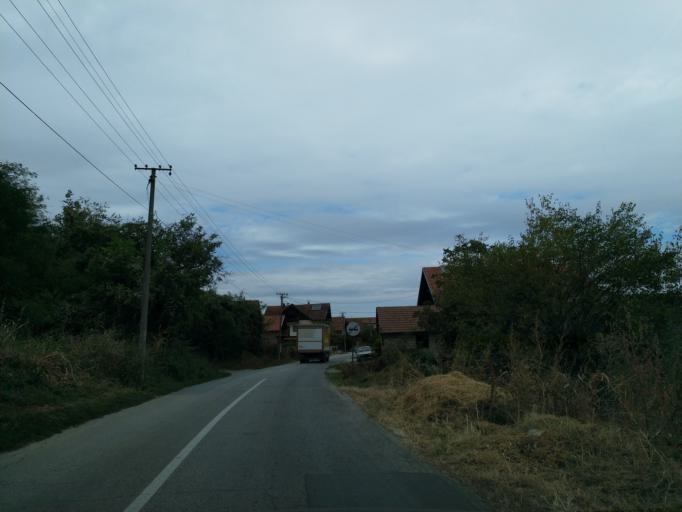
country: RS
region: Central Serbia
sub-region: Pomoravski Okrug
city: Cuprija
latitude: 43.8613
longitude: 21.3236
